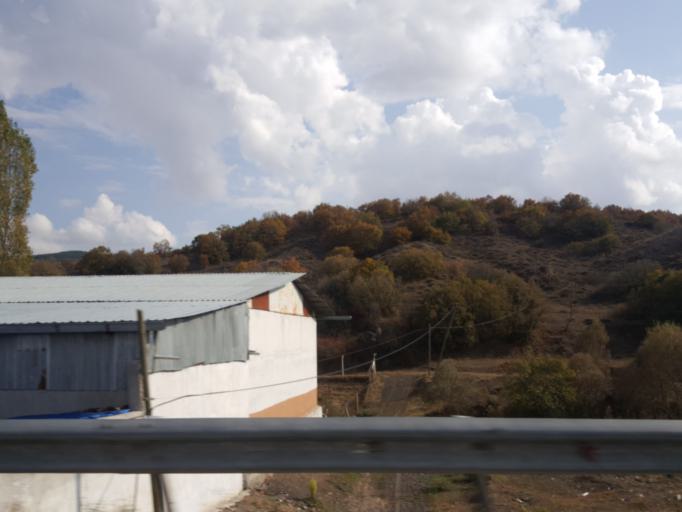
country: TR
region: Corum
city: Alaca
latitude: 40.3252
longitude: 34.7007
